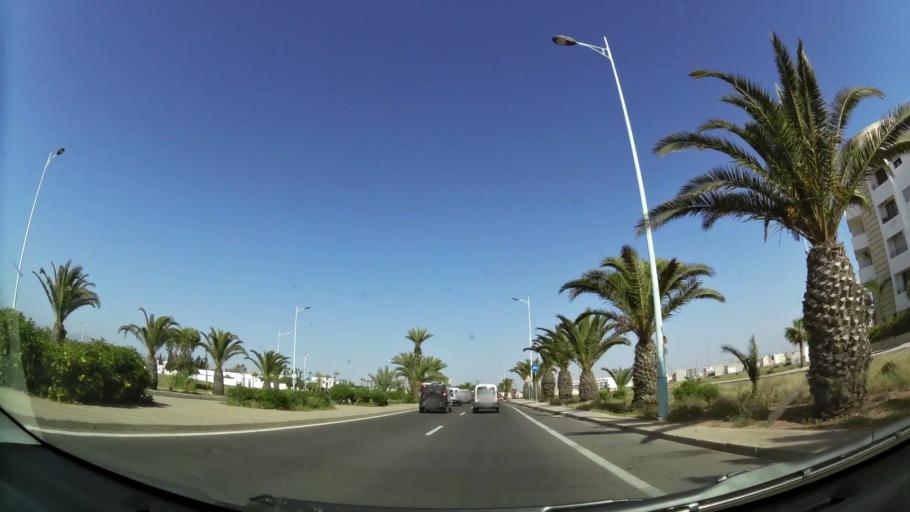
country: MA
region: Oued ed Dahab-Lagouira
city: Dakhla
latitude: 30.4032
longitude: -9.5737
